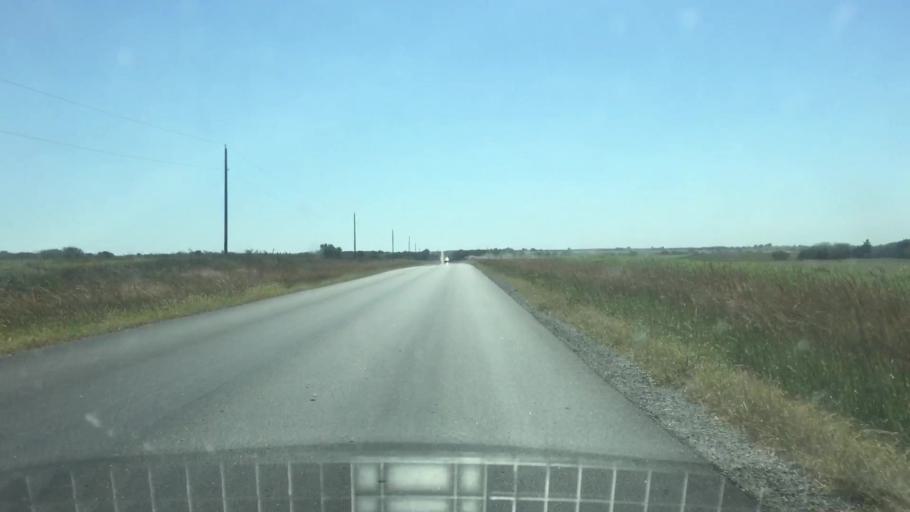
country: US
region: Kansas
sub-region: Marshall County
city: Marysville
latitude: 39.9496
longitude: -96.6008
